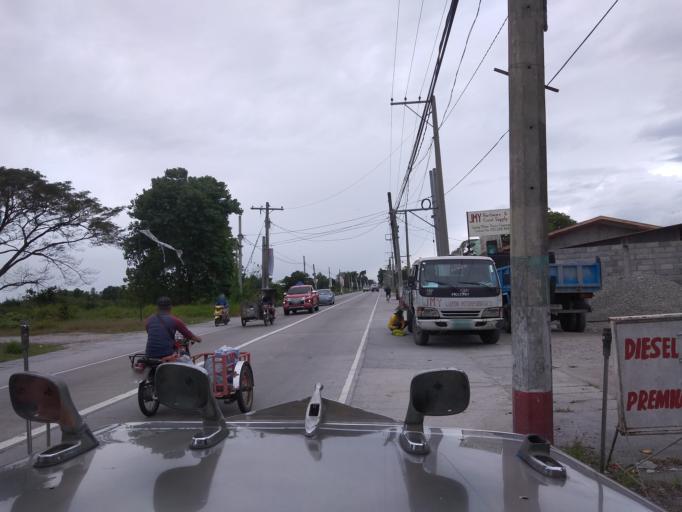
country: PH
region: Central Luzon
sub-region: Province of Pampanga
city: Pandacaqui
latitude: 15.1864
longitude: 120.6327
